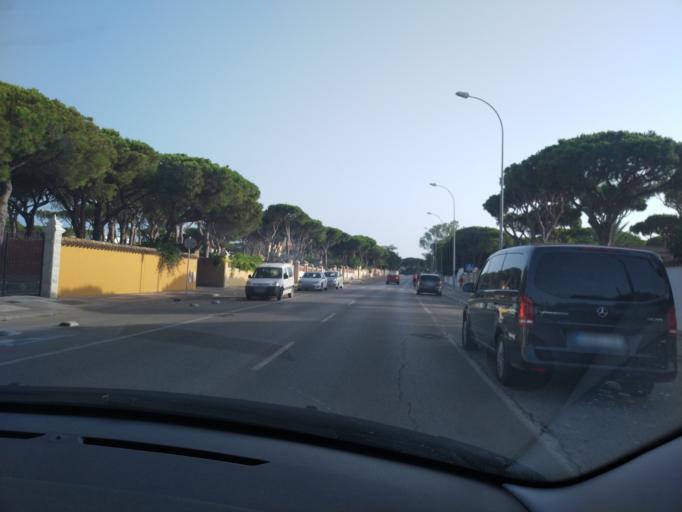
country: ES
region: Andalusia
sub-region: Provincia de Cadiz
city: Chiclana de la Frontera
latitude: 36.3829
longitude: -6.1901
